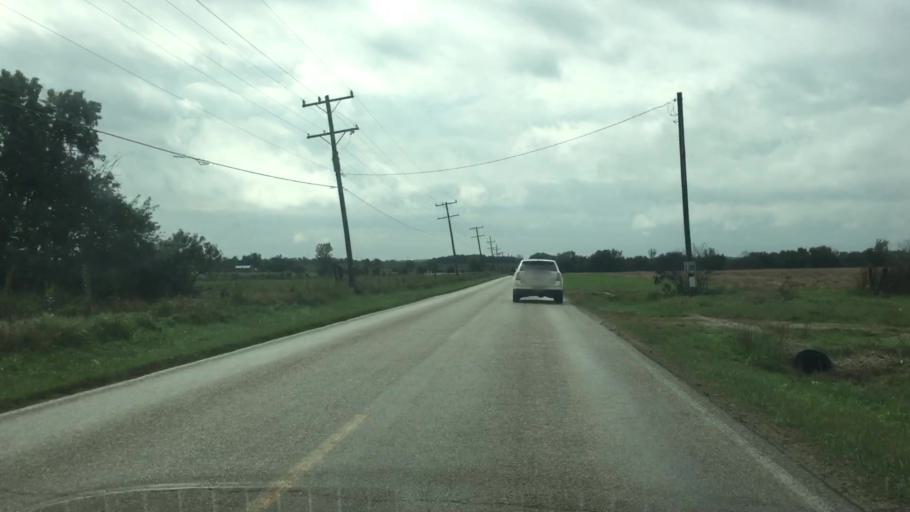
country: US
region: Kansas
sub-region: Allen County
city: Humboldt
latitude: 37.8568
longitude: -95.4369
